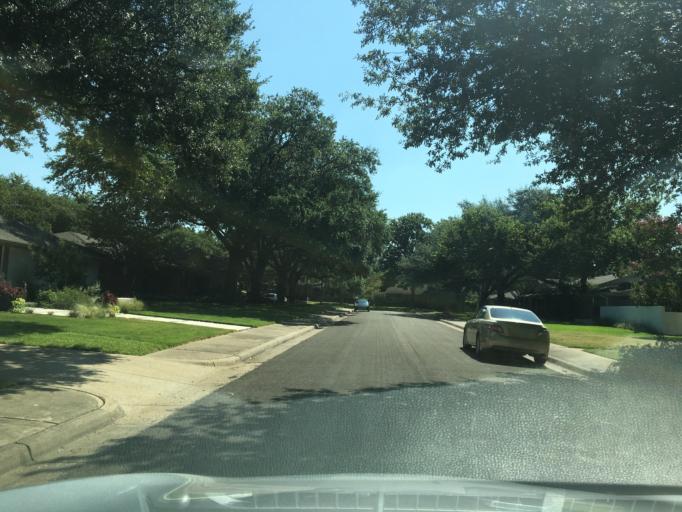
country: US
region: Texas
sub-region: Dallas County
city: Garland
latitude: 32.8626
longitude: -96.6905
